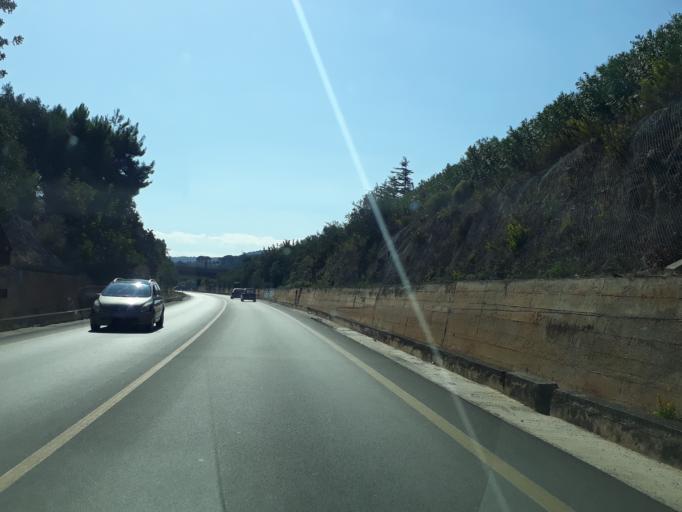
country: IT
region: Apulia
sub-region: Provincia di Brindisi
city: Fasano
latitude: 40.8365
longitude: 17.3504
